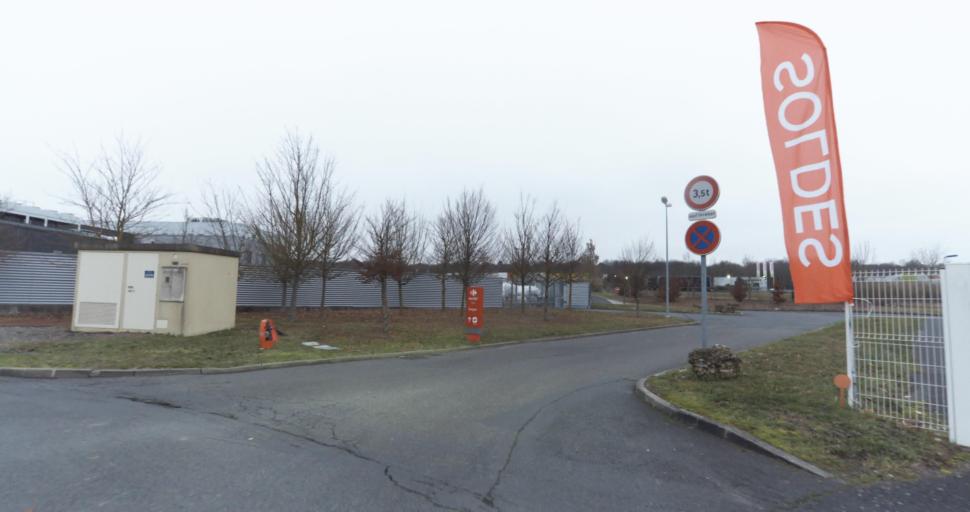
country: FR
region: Pays de la Loire
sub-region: Departement de Maine-et-Loire
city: Distre
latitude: 47.2325
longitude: -0.1143
